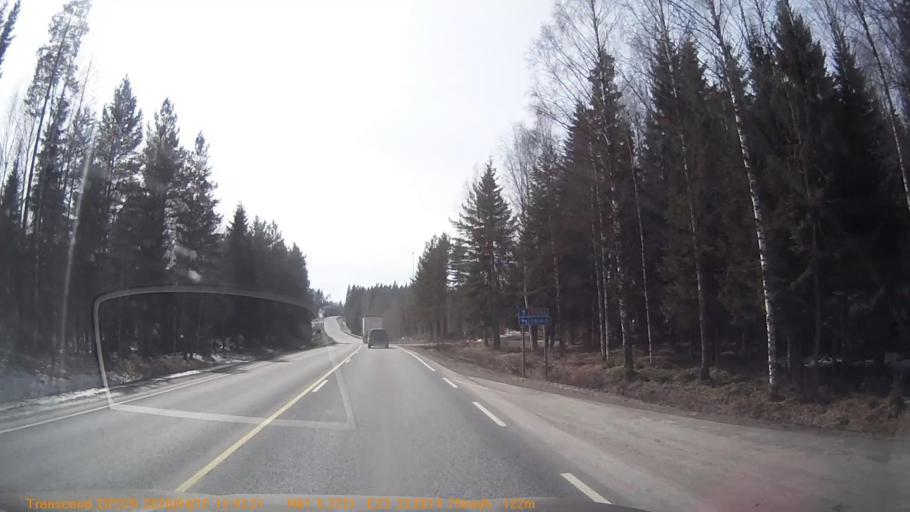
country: FI
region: Pirkanmaa
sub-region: Etelae-Pirkanmaa
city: Urjala
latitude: 61.0894
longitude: 23.5542
